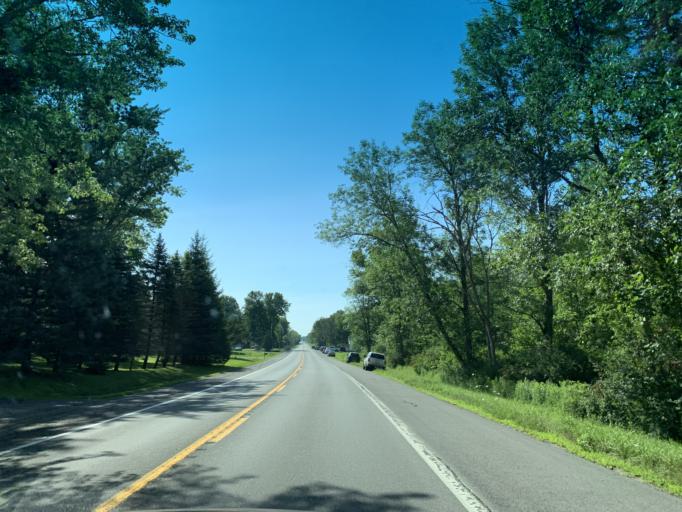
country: US
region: New York
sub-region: Madison County
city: Oneida
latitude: 43.1365
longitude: -75.6130
